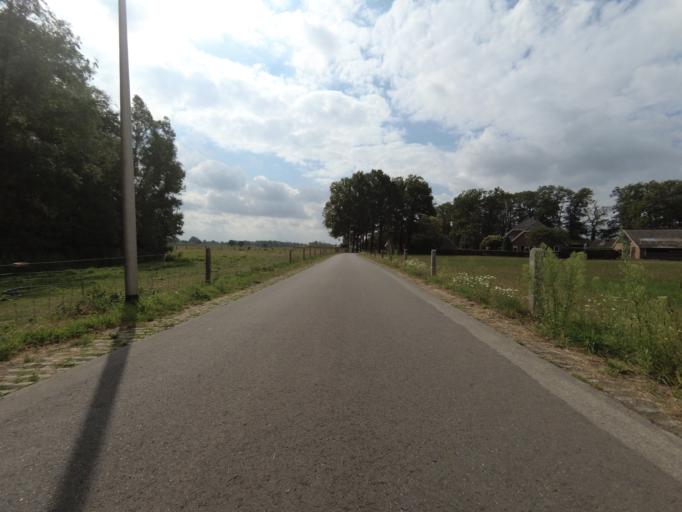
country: NL
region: Overijssel
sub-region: Gemeente Borne
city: Borne
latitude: 52.3155
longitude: 6.7149
